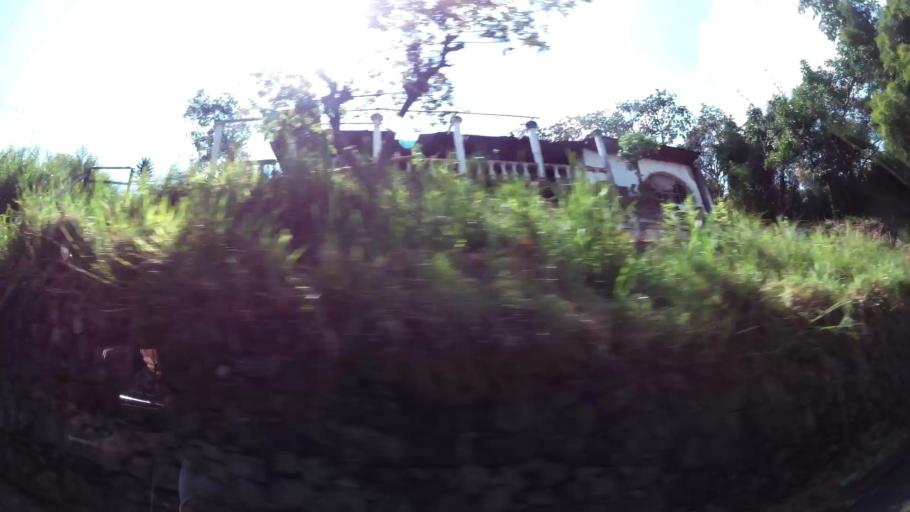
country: CO
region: Valle del Cauca
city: Cali
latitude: 3.4310
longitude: -76.5622
